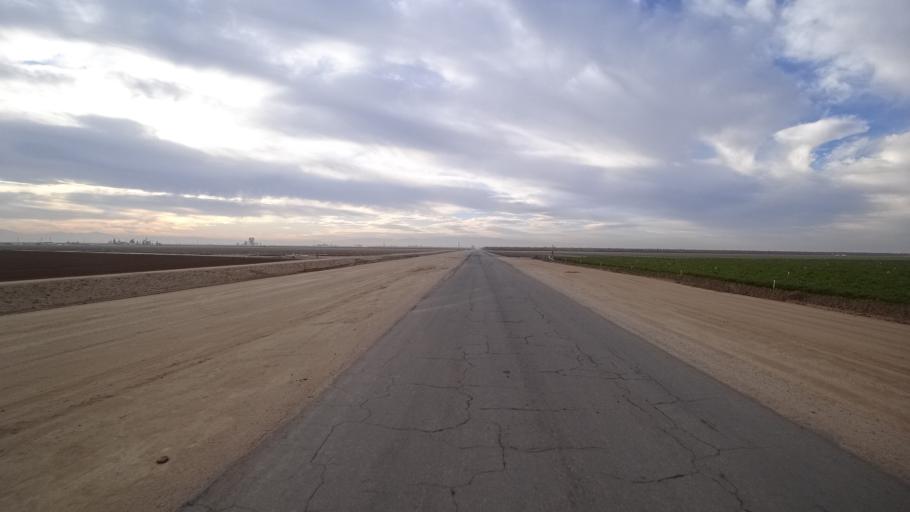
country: US
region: California
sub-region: Kern County
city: Rosedale
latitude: 35.4169
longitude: -119.1899
